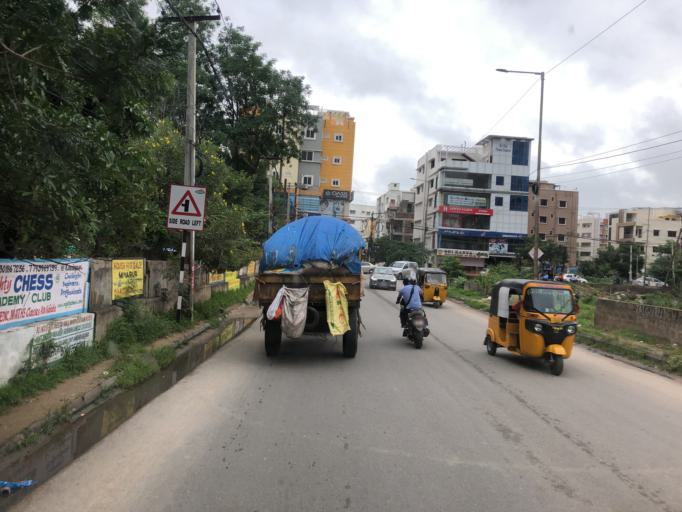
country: IN
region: Telangana
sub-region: Rangareddi
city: Kukatpalli
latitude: 17.4643
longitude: 78.3702
